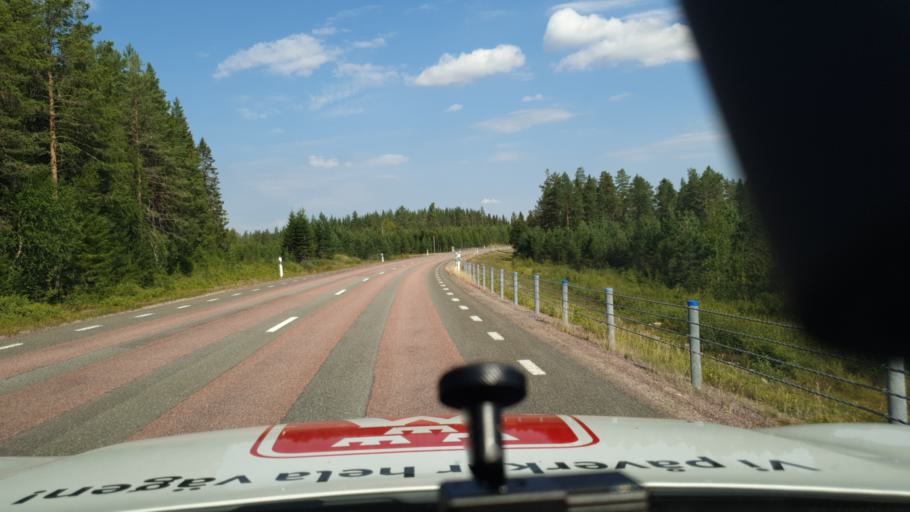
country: SE
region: Dalarna
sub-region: Malung-Saelens kommun
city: Malung
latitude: 60.5463
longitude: 13.5320
